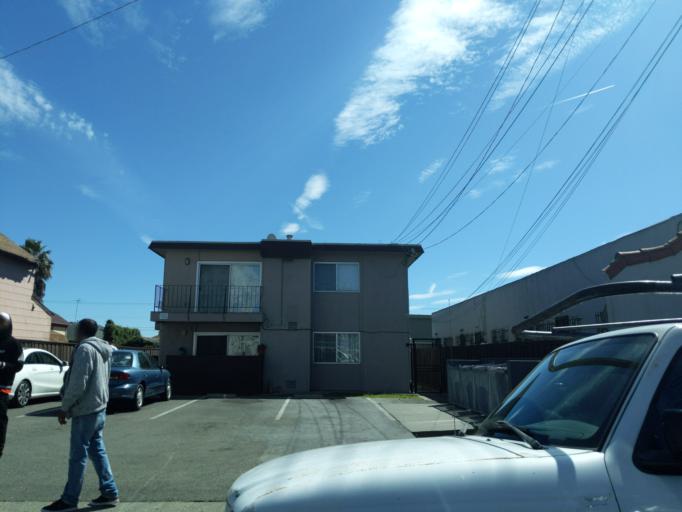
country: US
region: California
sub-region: Alameda County
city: Alameda
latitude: 37.7756
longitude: -122.2193
